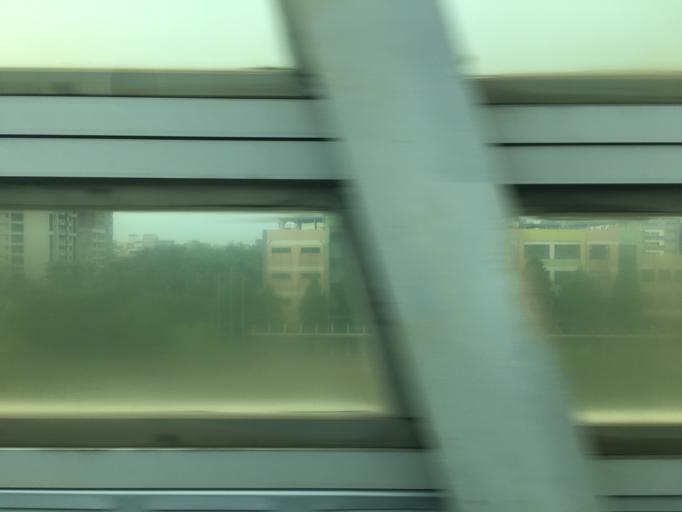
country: TW
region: Taiwan
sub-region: Taoyuan
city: Taoyuan
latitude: 25.0586
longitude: 121.3725
